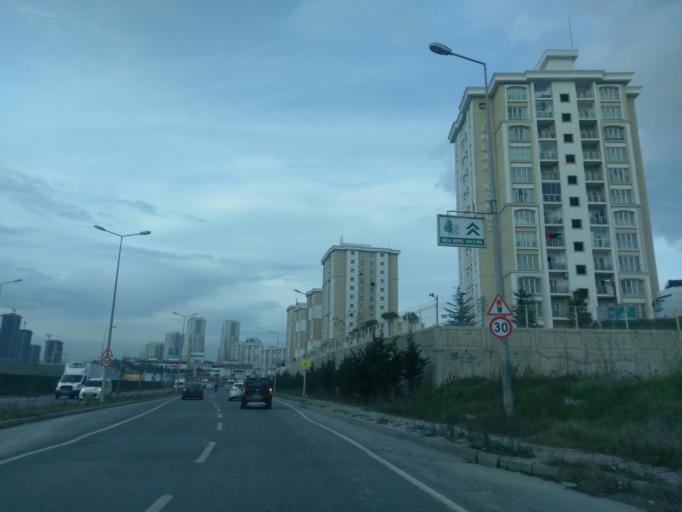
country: TR
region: Istanbul
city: Esenyurt
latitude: 41.0826
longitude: 28.6529
